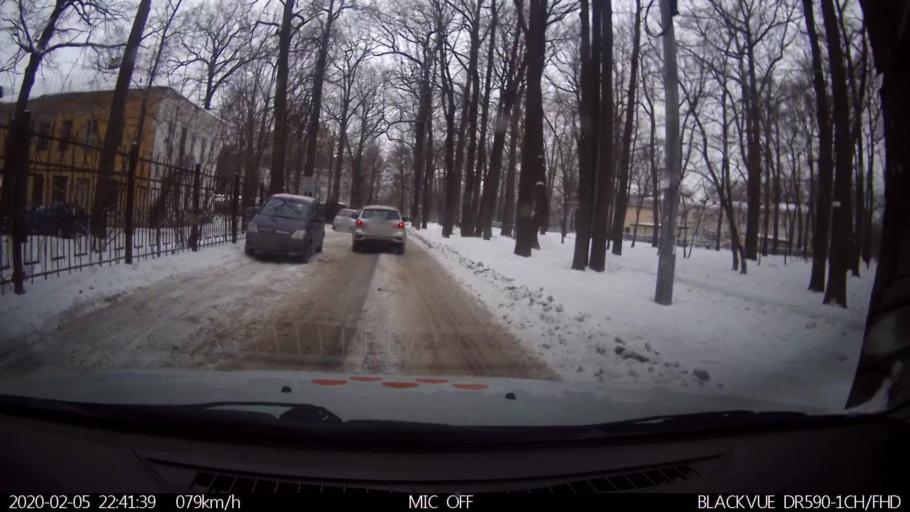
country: RU
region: Nizjnij Novgorod
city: Imeni Stepana Razina
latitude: 54.7202
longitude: 44.3424
